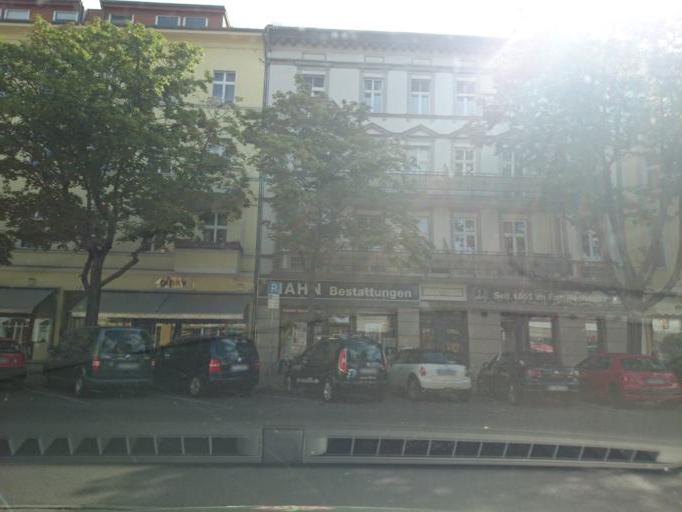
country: DE
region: Berlin
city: Lichterfelde
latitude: 52.4270
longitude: 13.3266
